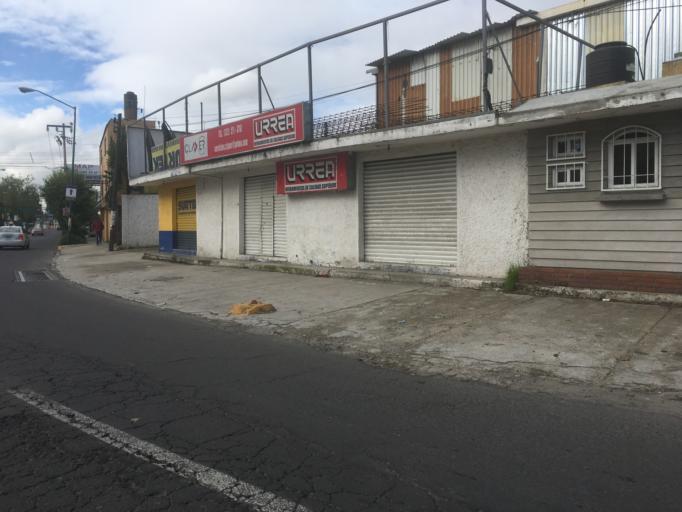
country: MX
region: Mexico
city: Santa Maria Totoltepec
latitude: 19.2867
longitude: -99.6103
